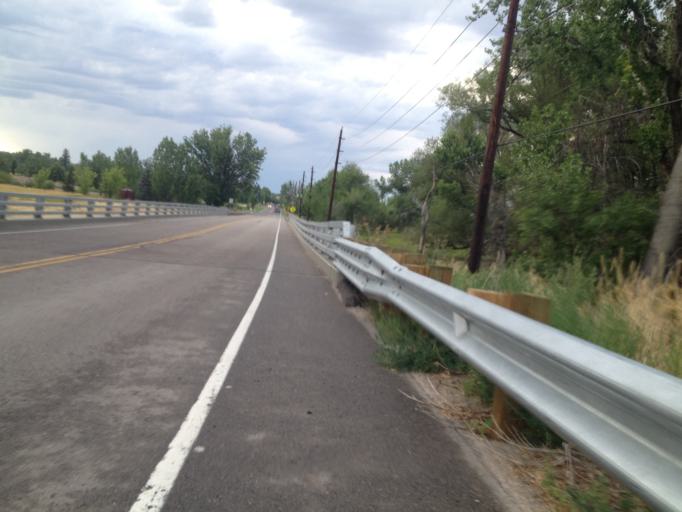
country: US
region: Colorado
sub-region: Boulder County
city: Louisville
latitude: 39.9688
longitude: -105.1284
